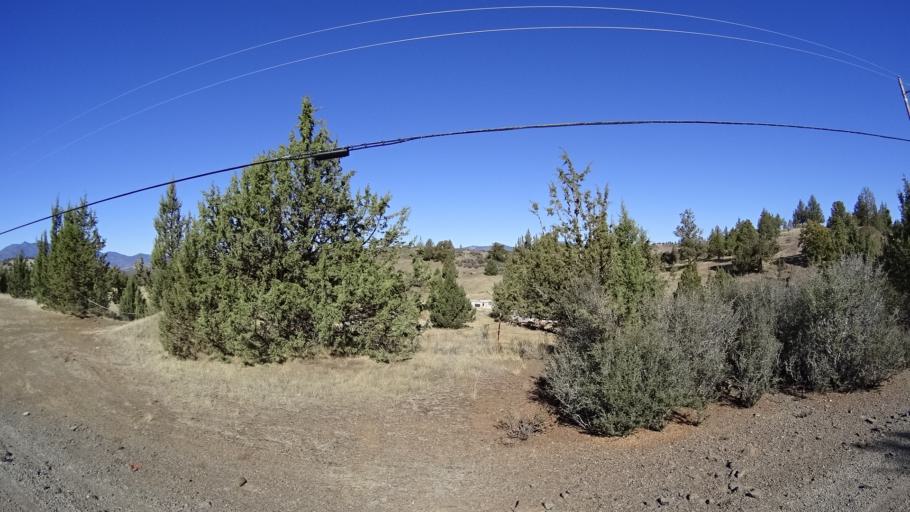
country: US
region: California
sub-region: Siskiyou County
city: Montague
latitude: 41.8829
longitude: -122.4125
